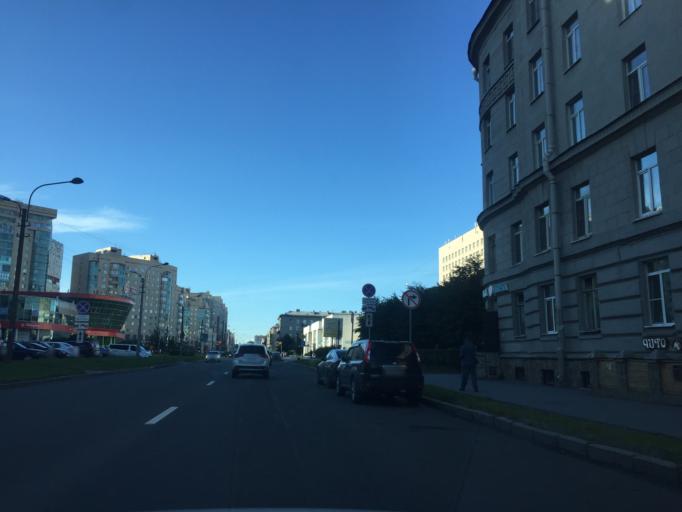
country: RU
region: St.-Petersburg
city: Kupchino
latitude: 59.8674
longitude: 30.3140
